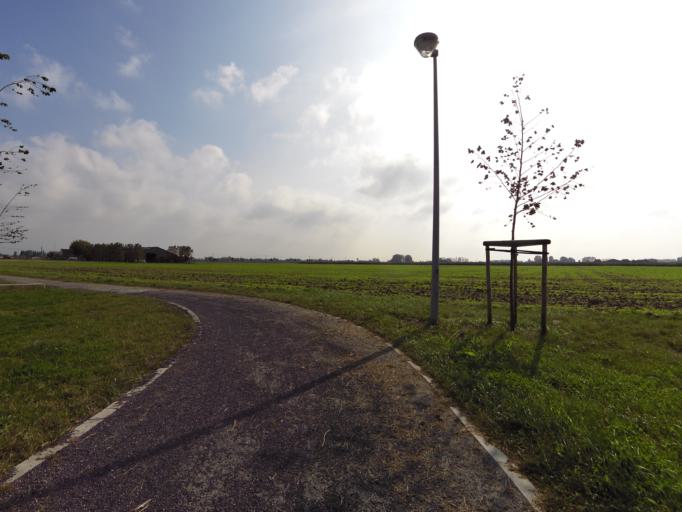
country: BE
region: Flanders
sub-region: Provincie West-Vlaanderen
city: Ostend
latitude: 51.1885
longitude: 2.8963
